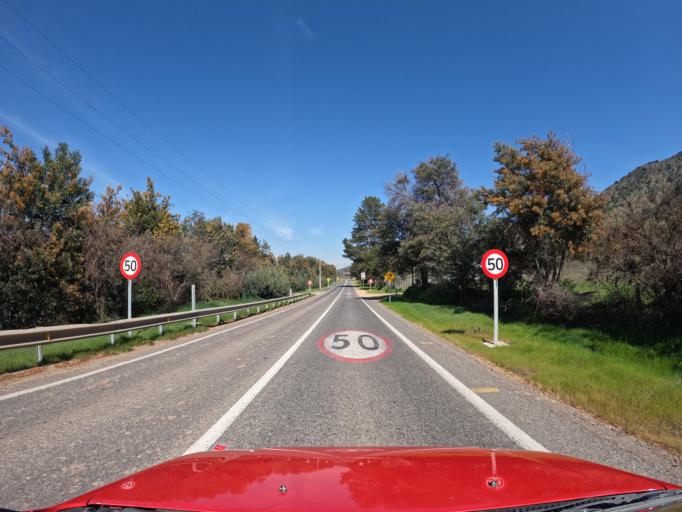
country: CL
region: Maule
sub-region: Provincia de Curico
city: Rauco
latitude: -35.0600
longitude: -71.6173
